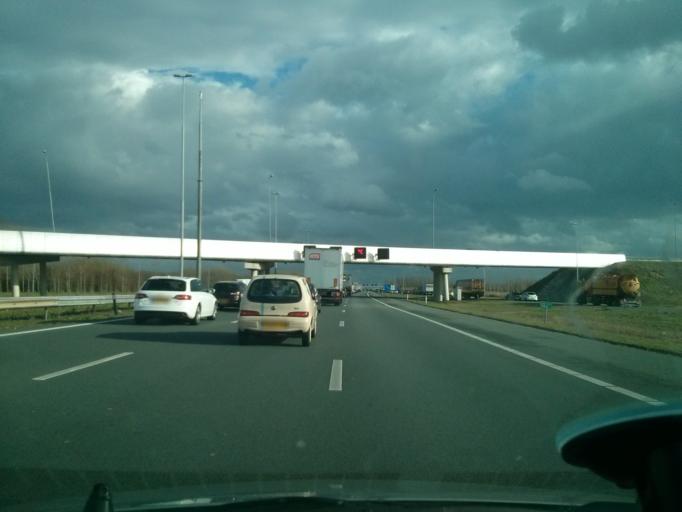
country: NL
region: Utrecht
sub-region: Gemeente Vianen
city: Vianen
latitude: 51.9745
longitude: 5.1045
